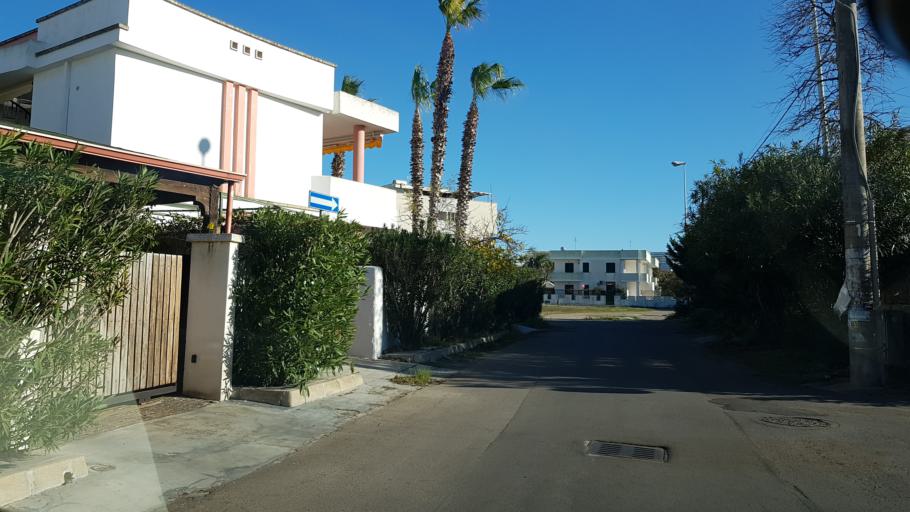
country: IT
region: Apulia
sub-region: Provincia di Lecce
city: Gallipoli
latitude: 40.0367
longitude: 18.0169
